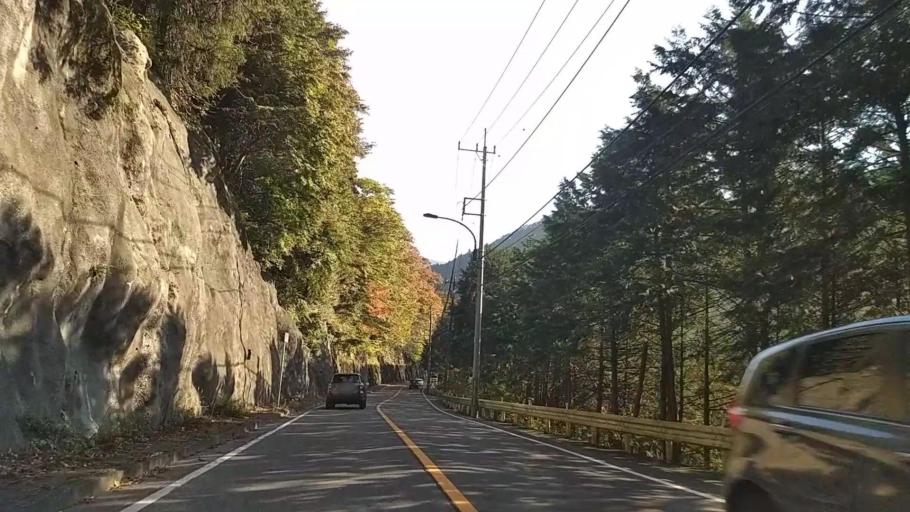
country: JP
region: Tokyo
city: Ome
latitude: 35.8100
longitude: 139.1687
